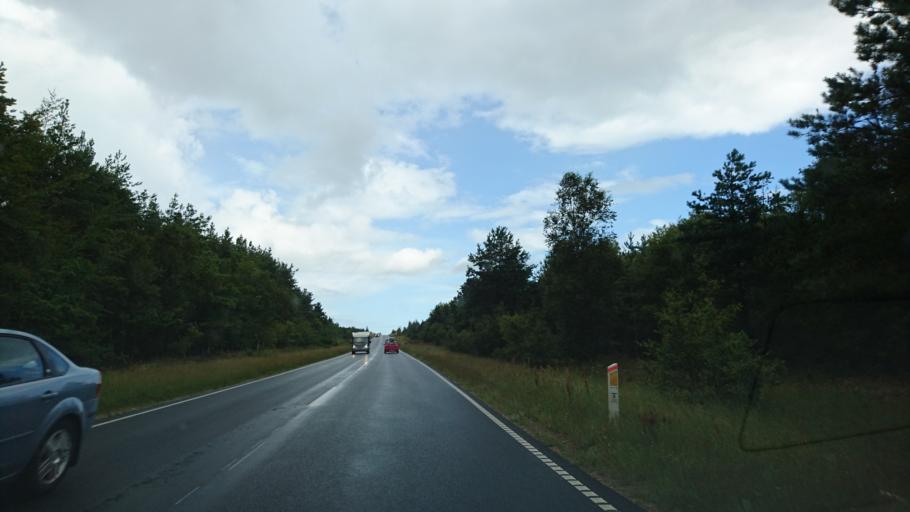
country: DK
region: North Denmark
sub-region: Frederikshavn Kommune
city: Skagen
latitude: 57.6488
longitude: 10.4609
